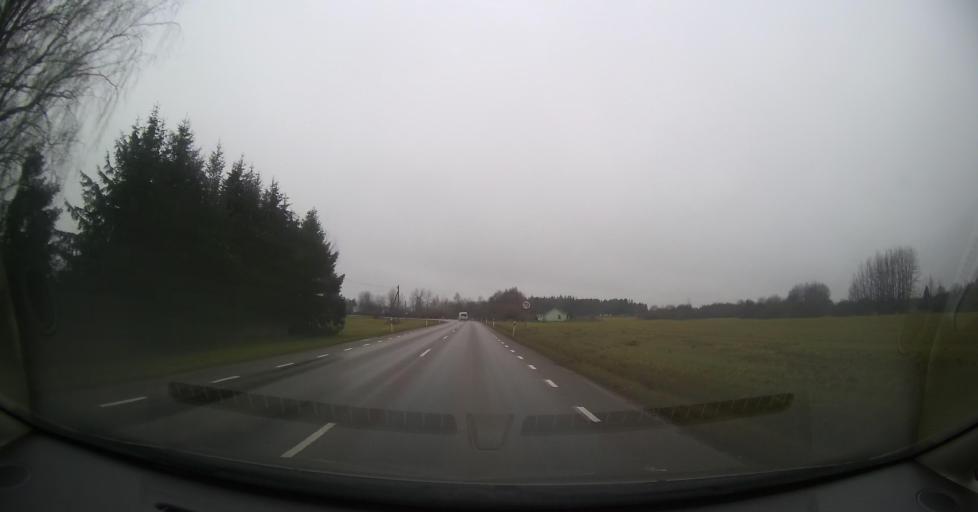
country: EE
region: Tartu
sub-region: Tartu linn
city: Tartu
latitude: 58.3832
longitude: 26.7851
